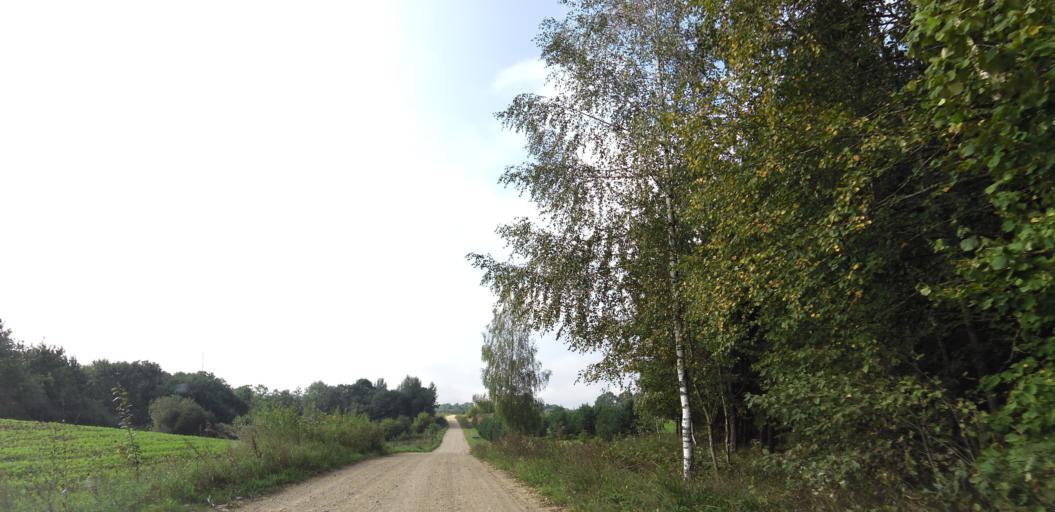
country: LT
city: Grigiskes
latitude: 54.7705
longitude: 25.0551
